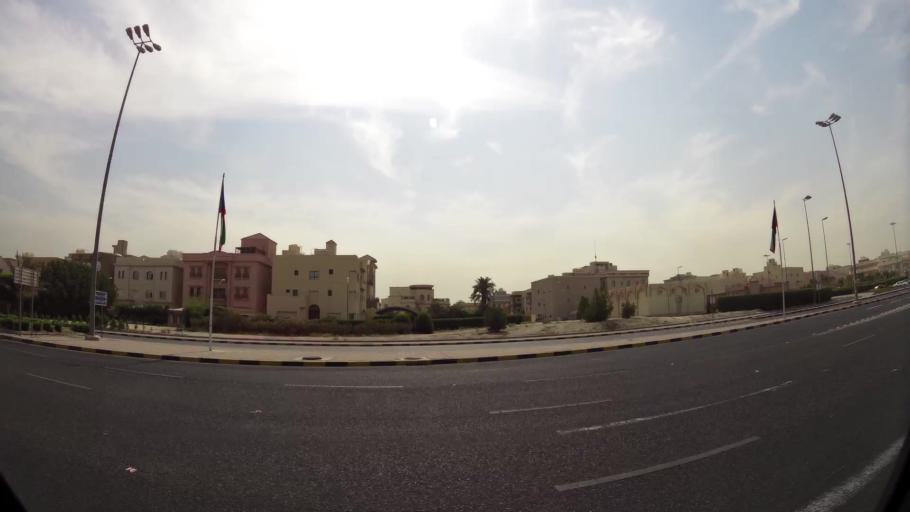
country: KW
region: Al Farwaniyah
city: Janub as Surrah
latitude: 29.2857
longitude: 47.9950
